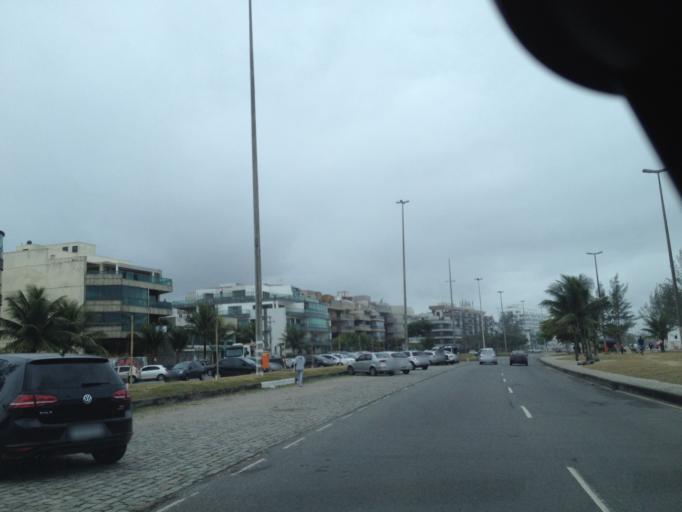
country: BR
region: Rio de Janeiro
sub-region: Nilopolis
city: Nilopolis
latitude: -23.0297
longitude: -43.4687
